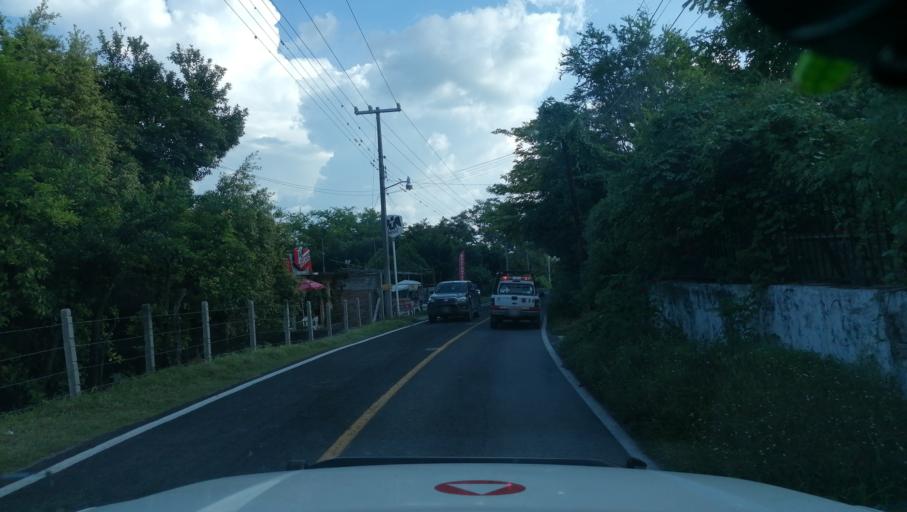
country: MX
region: Morelos
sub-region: Ayala
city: Abelardo L. Rodriguez
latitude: 18.7163
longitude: -98.9903
